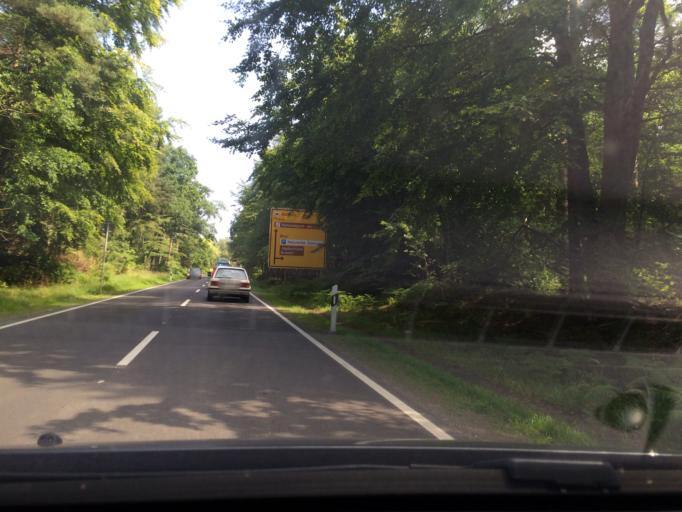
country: DE
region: Mecklenburg-Vorpommern
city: Ostseebad Binz
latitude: 54.4381
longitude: 13.5632
